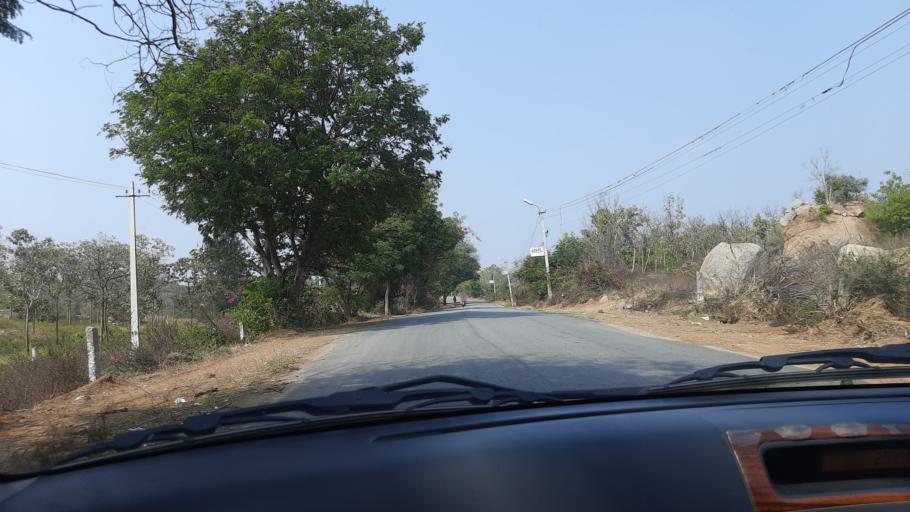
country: IN
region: Telangana
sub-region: Rangareddi
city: Lal Bahadur Nagar
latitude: 17.2756
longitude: 78.6580
